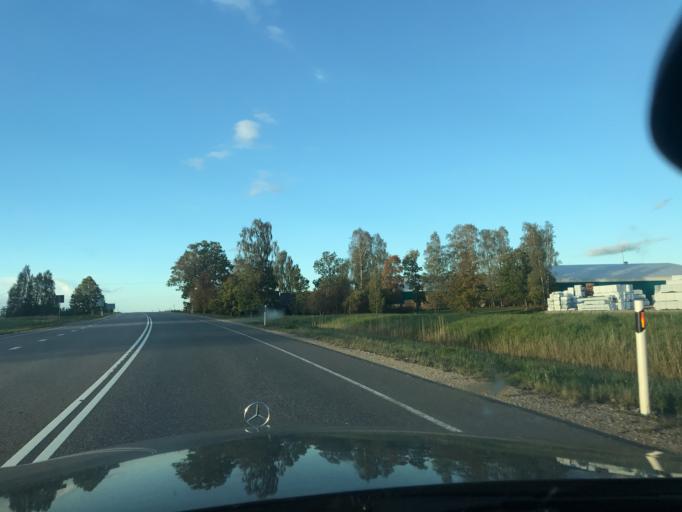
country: EE
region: Vorumaa
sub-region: Voru linn
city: Voru
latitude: 57.8109
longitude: 27.0650
